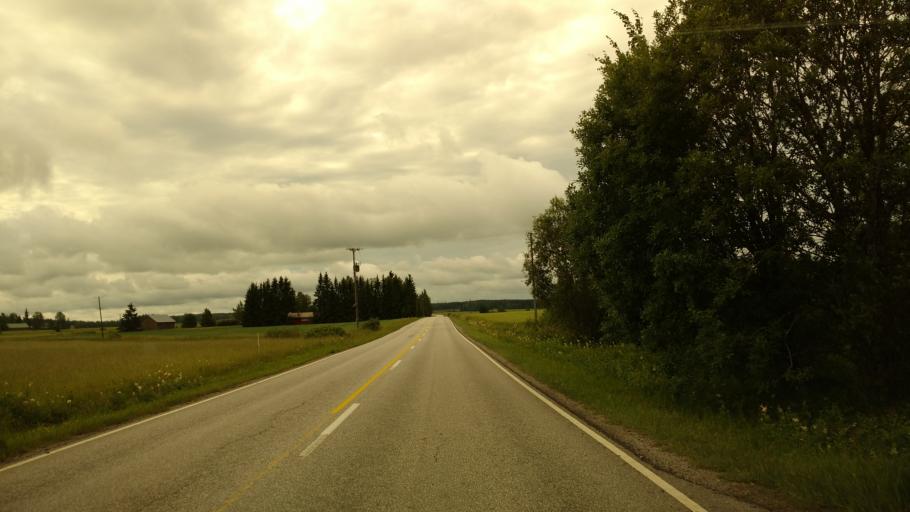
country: FI
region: Varsinais-Suomi
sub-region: Salo
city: Kuusjoki
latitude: 60.4802
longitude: 23.1604
